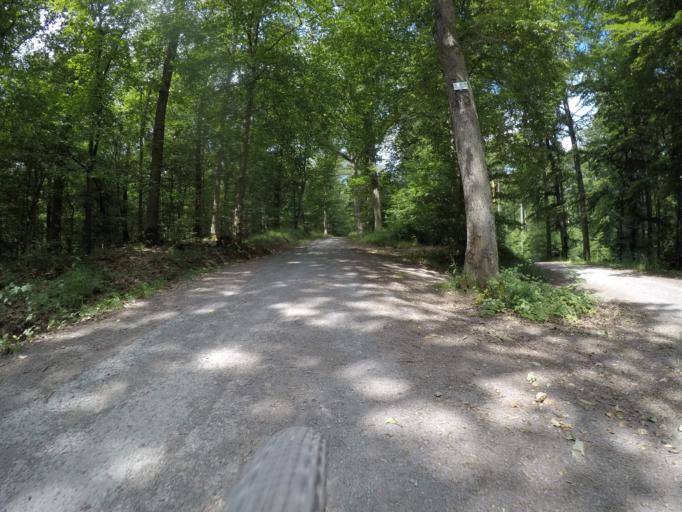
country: DE
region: Baden-Wuerttemberg
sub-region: Regierungsbezirk Stuttgart
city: Stuttgart Feuerbach
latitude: 48.7884
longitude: 9.1242
